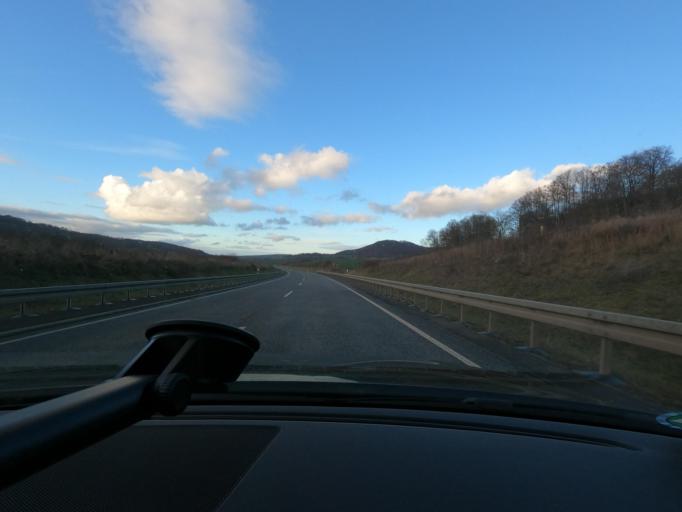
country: DE
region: Thuringia
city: Worbis
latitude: 51.4333
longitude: 10.3382
